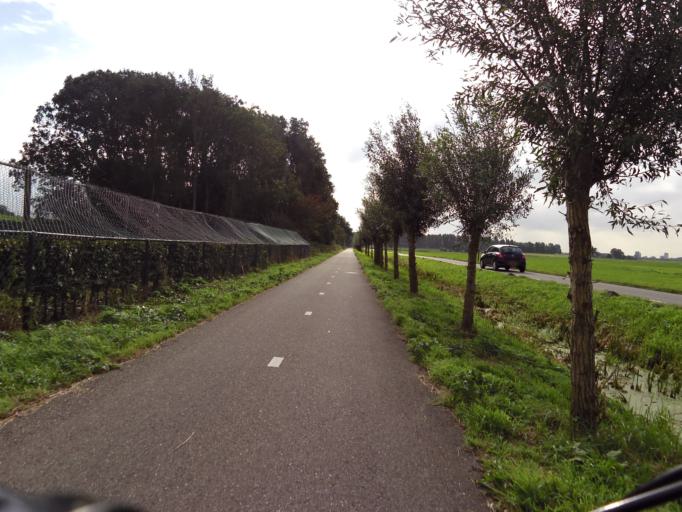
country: NL
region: South Holland
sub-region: Gemeente Zoetermeer
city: Zoetermeer
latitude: 52.0997
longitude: 4.4997
